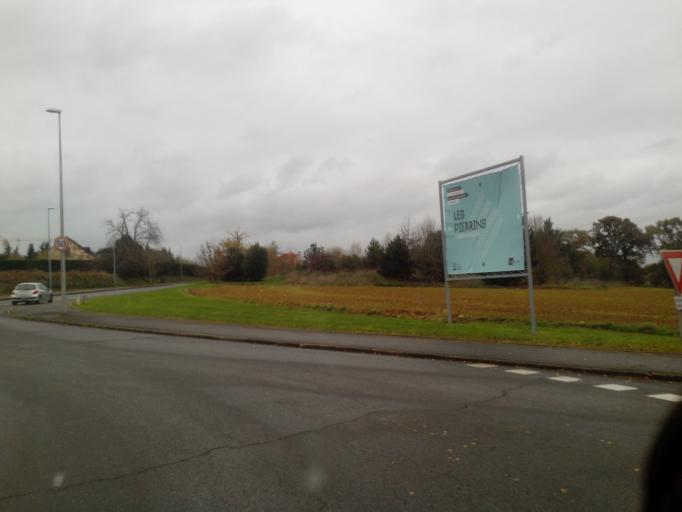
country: FR
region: Brittany
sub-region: Departement d'Ille-et-Vilaine
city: Cesson-Sevigne
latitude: 48.1271
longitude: -1.6133
